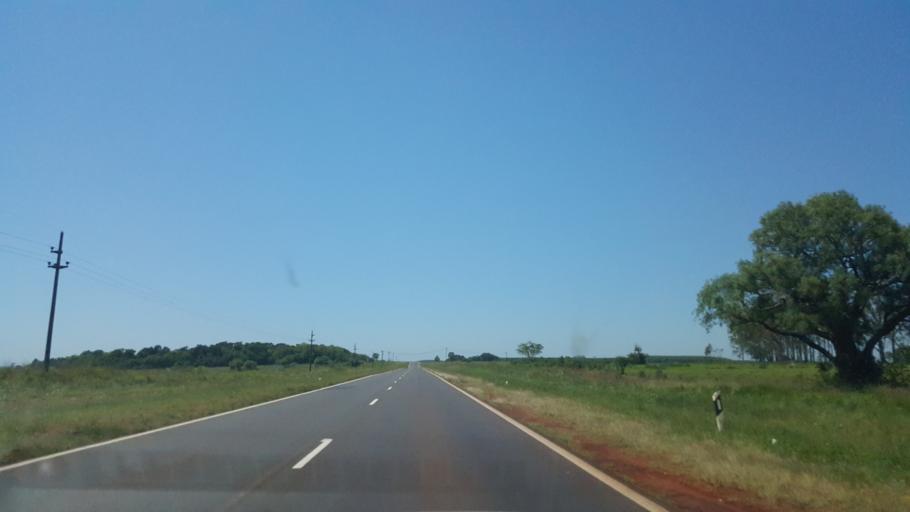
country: AR
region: Corrientes
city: Santo Tome
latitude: -28.3678
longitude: -56.1106
